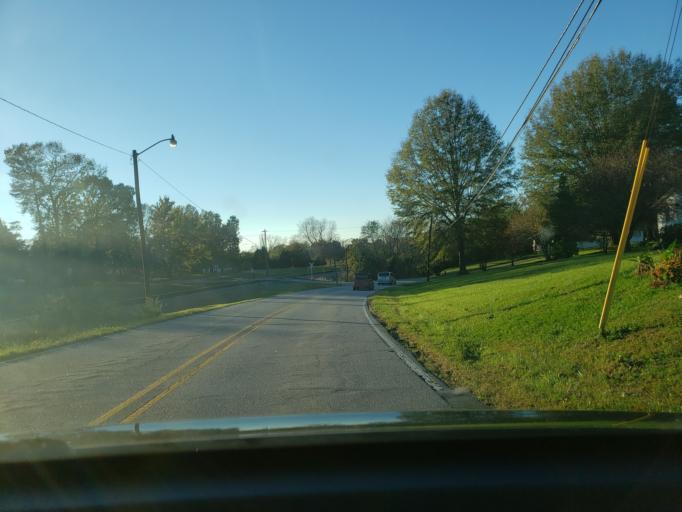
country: US
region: North Carolina
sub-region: Forsyth County
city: Walkertown
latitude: 36.1833
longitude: -80.1578
